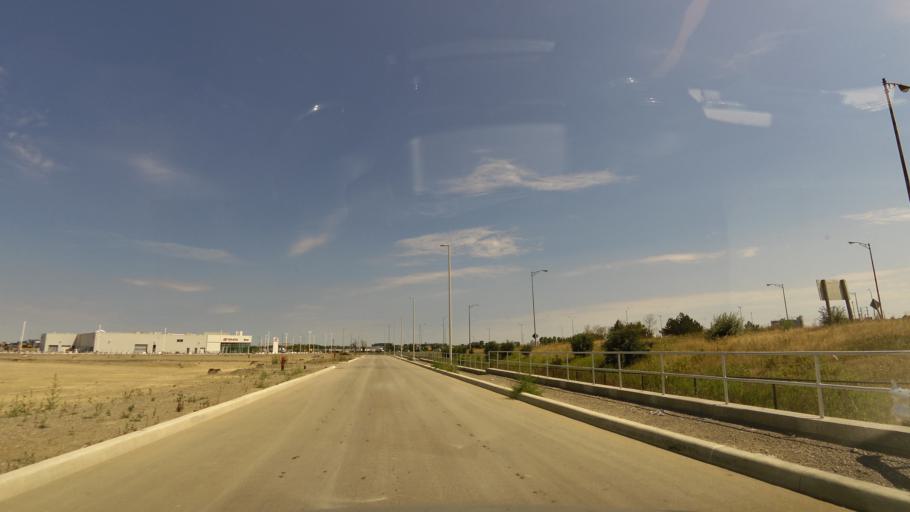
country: CA
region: Ontario
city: Etobicoke
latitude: 43.6505
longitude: -79.6381
